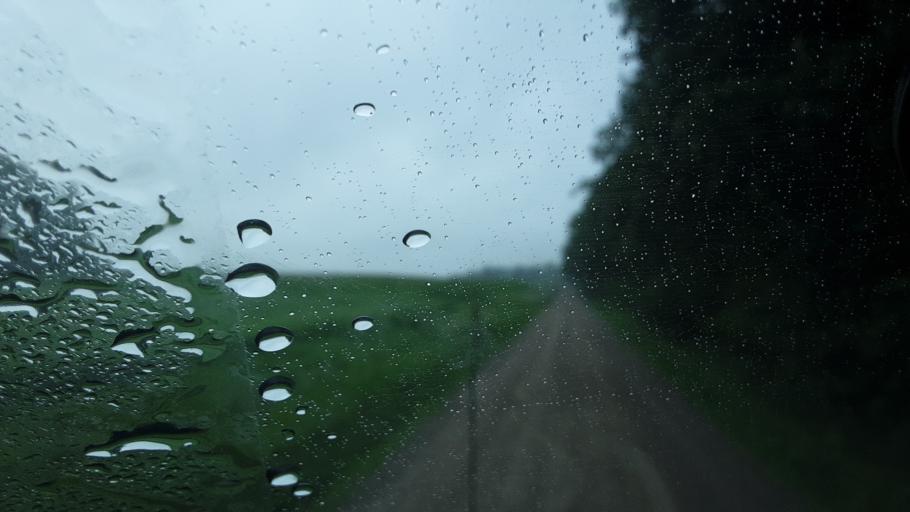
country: US
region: Indiana
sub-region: Adams County
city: Berne
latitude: 40.6373
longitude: -84.9835
